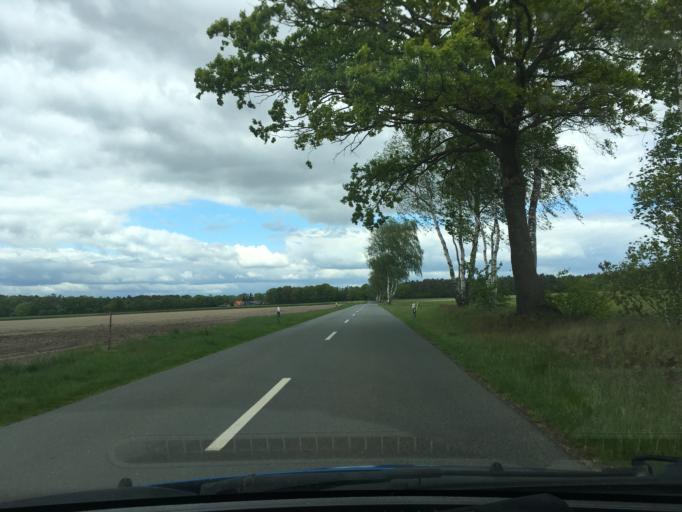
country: DE
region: Lower Saxony
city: Gerdau
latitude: 52.9426
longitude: 10.4031
